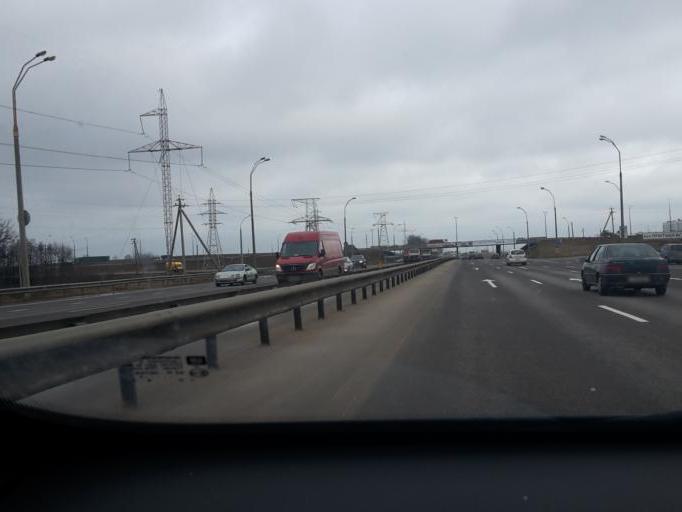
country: BY
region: Minsk
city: Zhdanovichy
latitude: 53.9080
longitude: 27.4084
